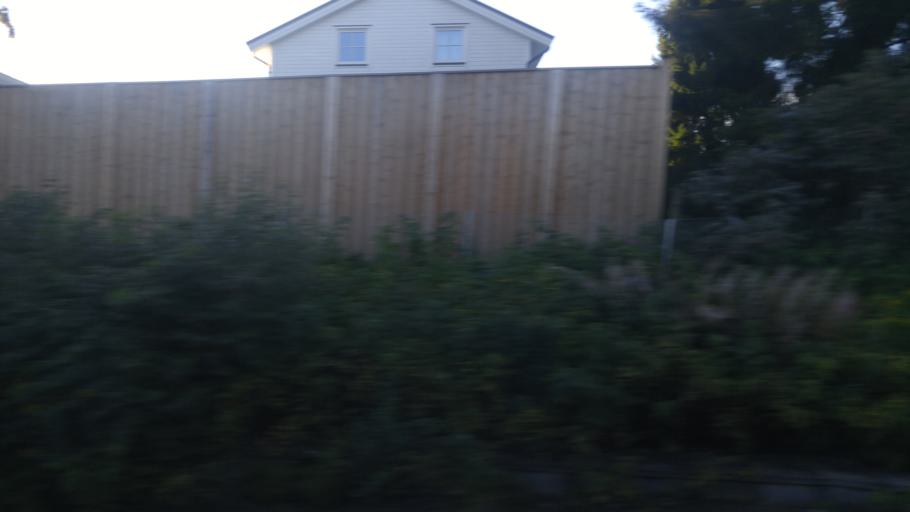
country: NO
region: Akershus
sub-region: Skedsmo
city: Lillestrom
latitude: 59.9515
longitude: 11.0042
